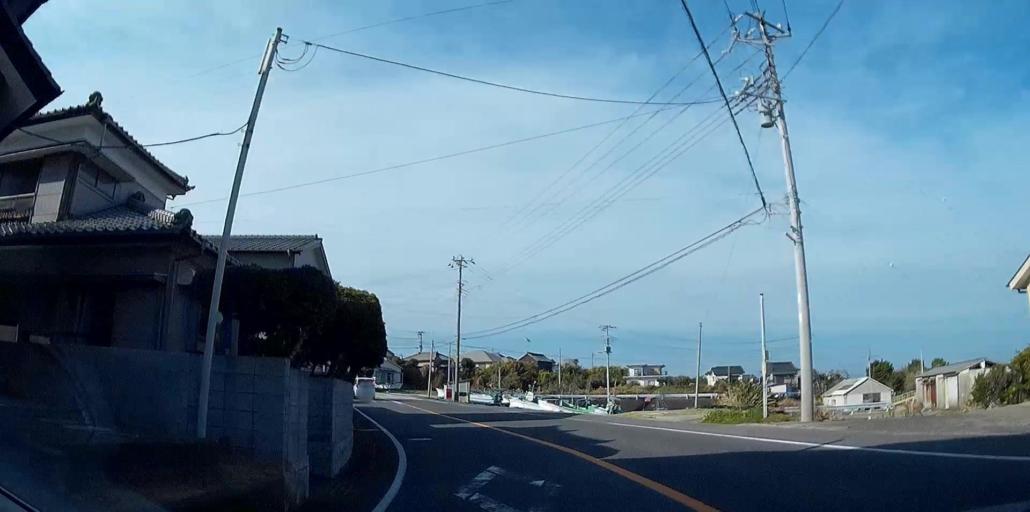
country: JP
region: Chiba
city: Tateyama
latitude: 34.9455
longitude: 139.9636
